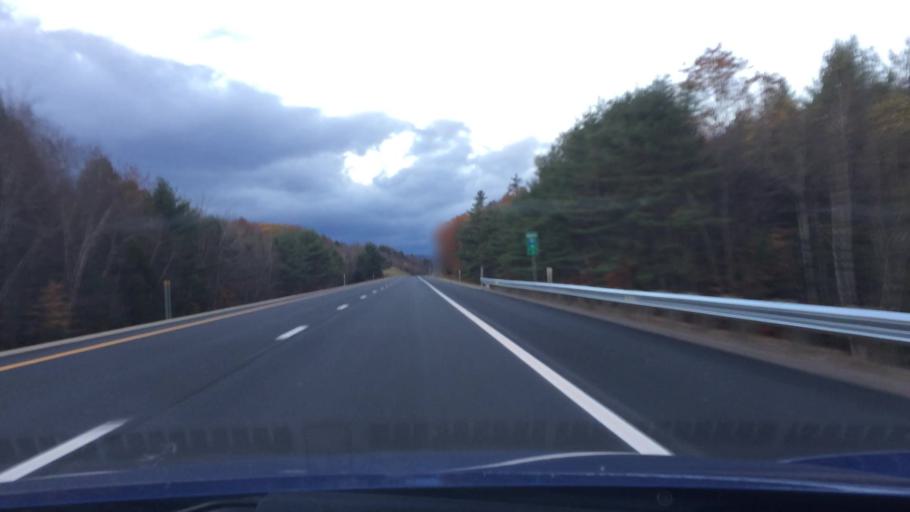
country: US
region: New Hampshire
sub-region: Grafton County
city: Thornton
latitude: 43.8825
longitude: -71.6773
